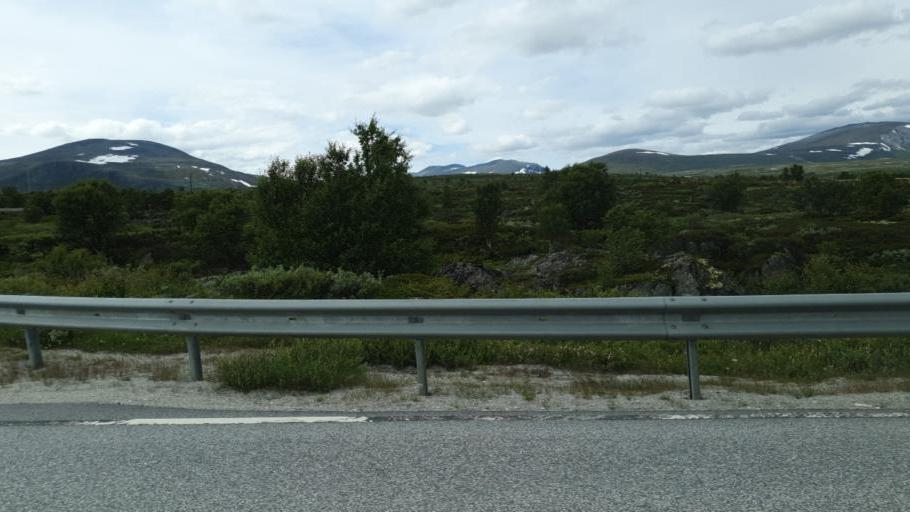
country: NO
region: Sor-Trondelag
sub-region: Oppdal
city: Oppdal
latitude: 62.2676
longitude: 9.5825
